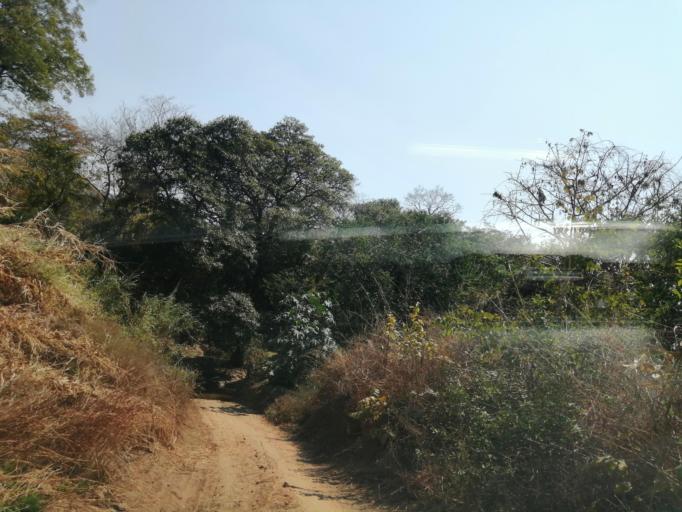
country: ZM
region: Eastern
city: Nyimba
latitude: -14.3344
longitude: 30.0309
